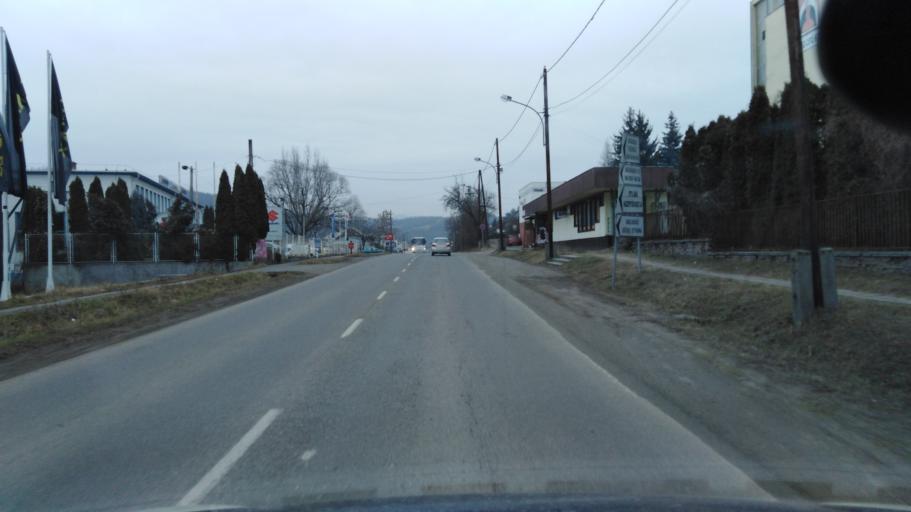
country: HU
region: Nograd
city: Salgotarjan
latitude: 48.0840
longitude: 19.7934
